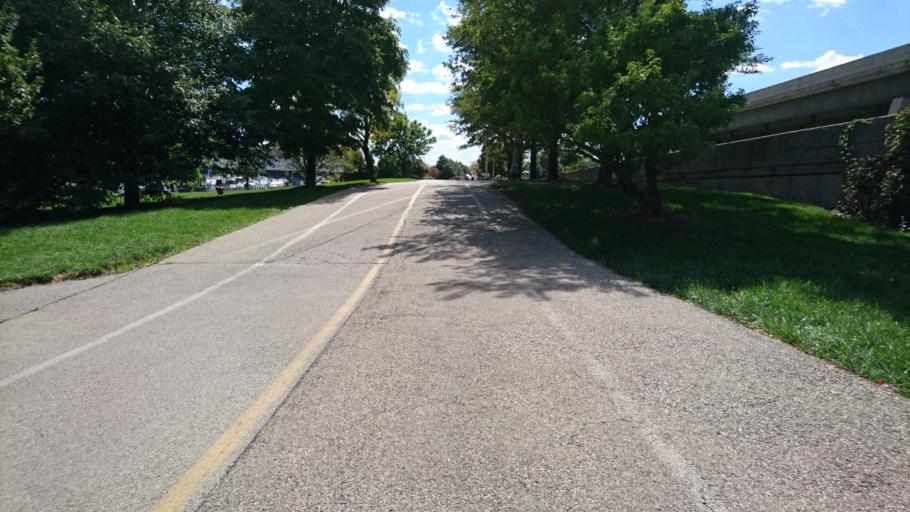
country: US
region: Illinois
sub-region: Cook County
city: Chicago
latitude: 41.8859
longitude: -87.6134
